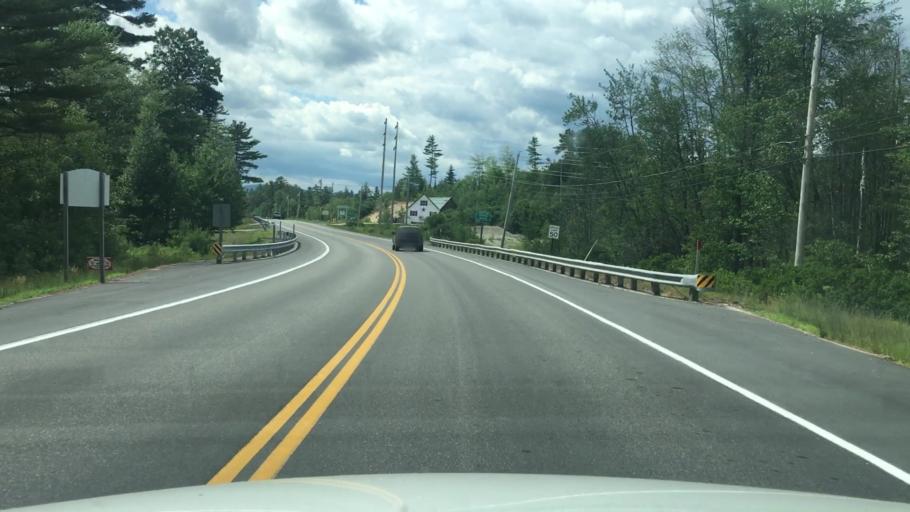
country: US
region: Maine
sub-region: Oxford County
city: Bethel
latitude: 44.4036
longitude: -70.7082
